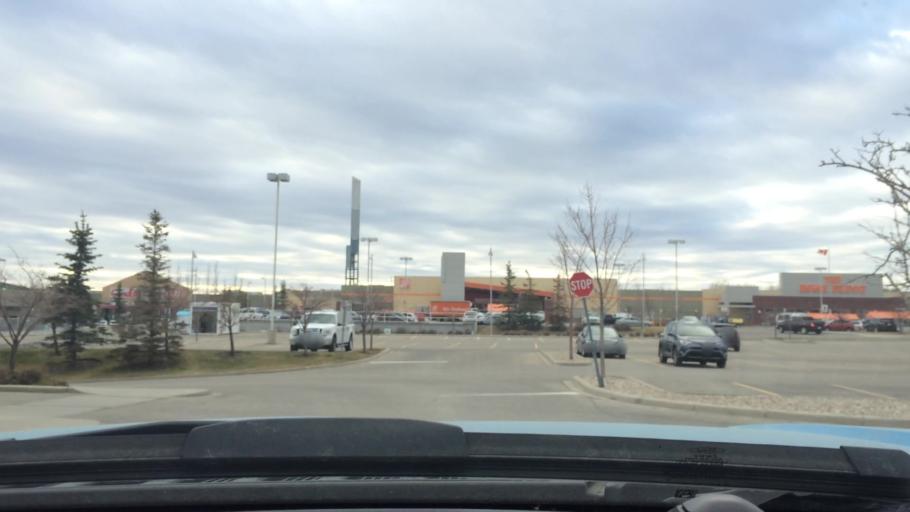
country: CA
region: Alberta
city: Calgary
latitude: 51.1565
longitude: -114.1606
